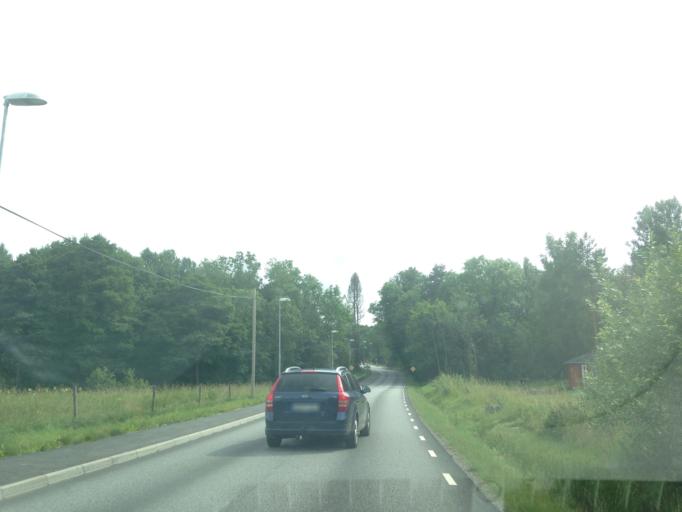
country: SE
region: Vaestra Goetaland
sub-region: Goteborg
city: Goeteborg
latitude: 57.7687
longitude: 11.9501
